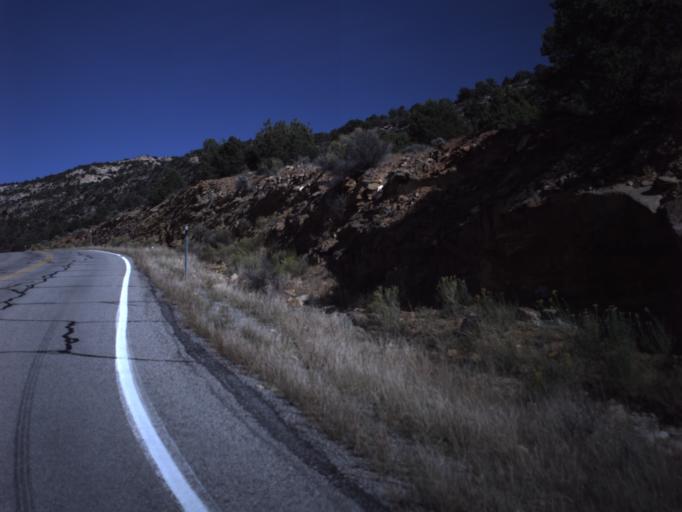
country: US
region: Utah
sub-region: San Juan County
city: Monticello
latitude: 37.9836
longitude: -109.5031
